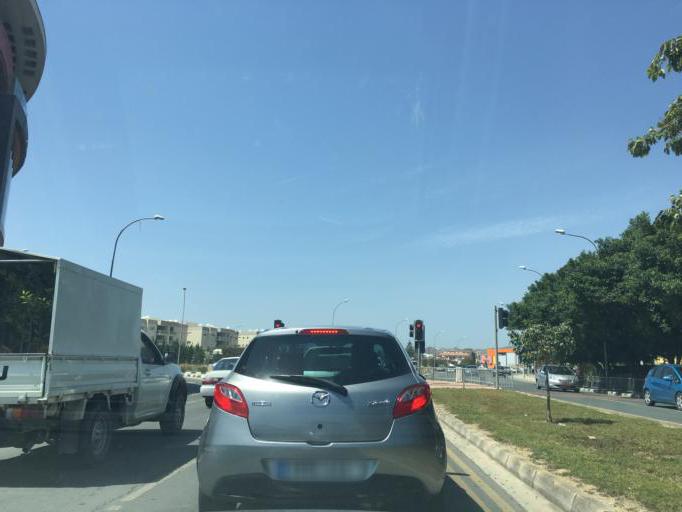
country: CY
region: Limassol
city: Limassol
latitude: 34.6998
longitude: 33.0610
